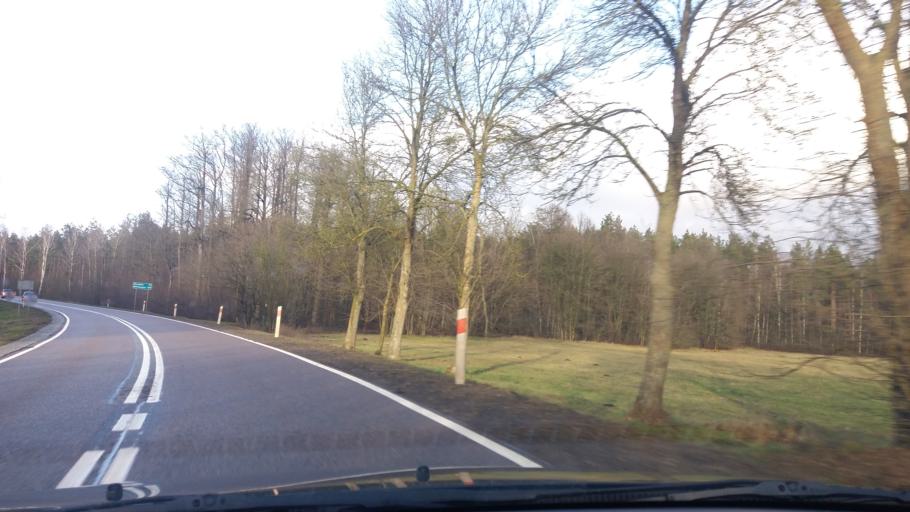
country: PL
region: Warmian-Masurian Voivodeship
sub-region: Powiat szczycienski
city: Wielbark
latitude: 53.4195
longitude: 20.9598
